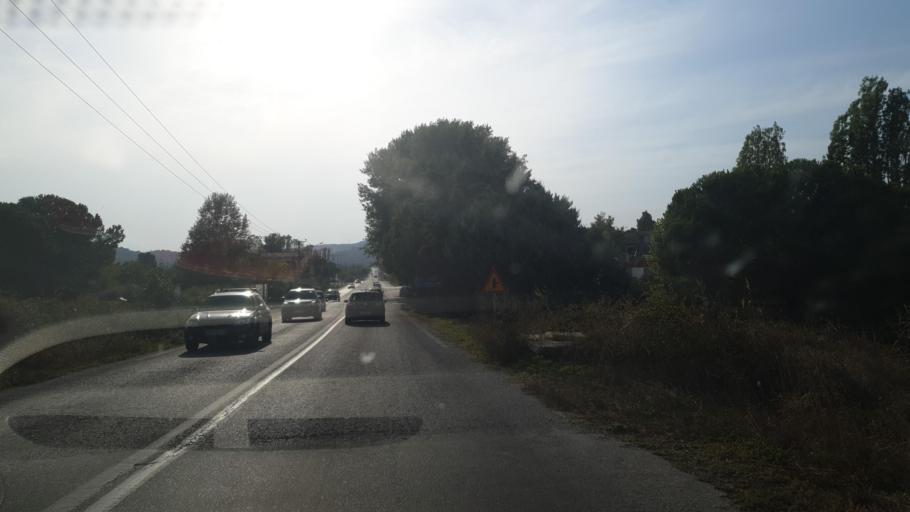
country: GR
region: Central Macedonia
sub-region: Nomos Chalkidikis
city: Agios Nikolaos
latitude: 40.2331
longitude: 23.7319
